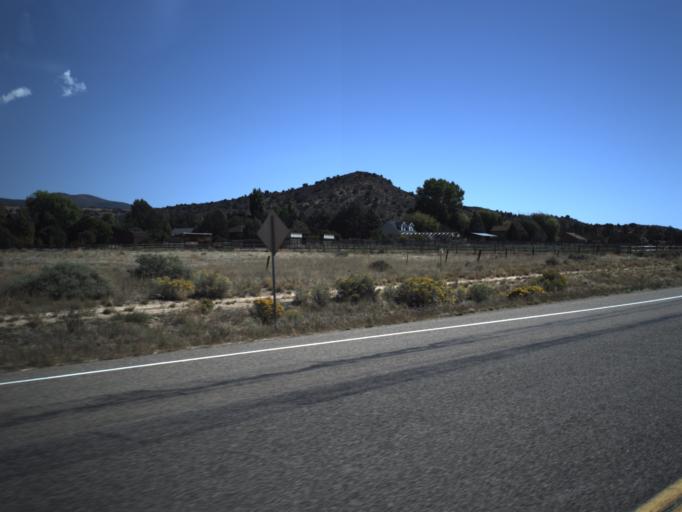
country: US
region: Utah
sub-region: Washington County
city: Ivins
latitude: 37.3040
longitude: -113.6696
